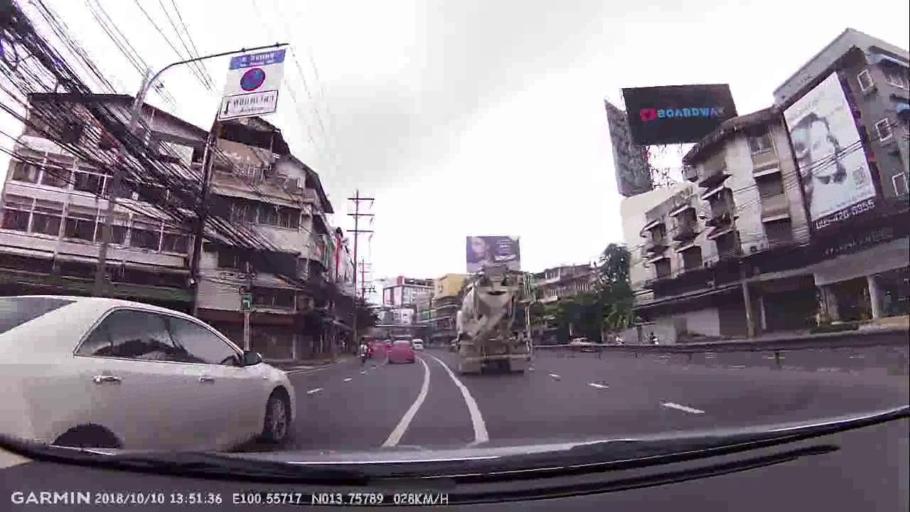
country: TH
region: Bangkok
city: Din Daeng
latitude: 13.7579
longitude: 100.5572
